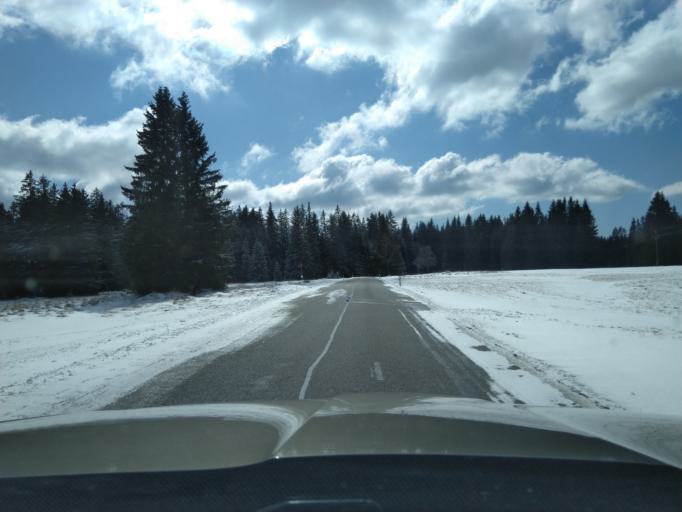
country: CZ
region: Jihocesky
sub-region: Okres Prachatice
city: Borova Lada
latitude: 49.0438
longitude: 13.5784
